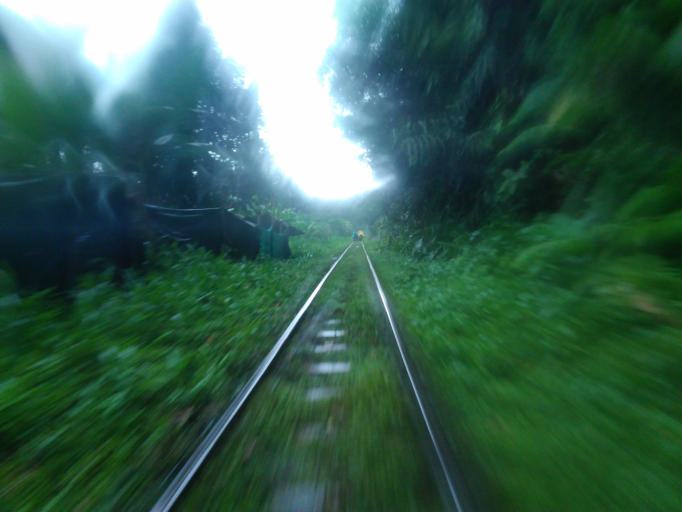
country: CO
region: Valle del Cauca
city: Buenaventura
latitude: 3.8485
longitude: -76.8617
